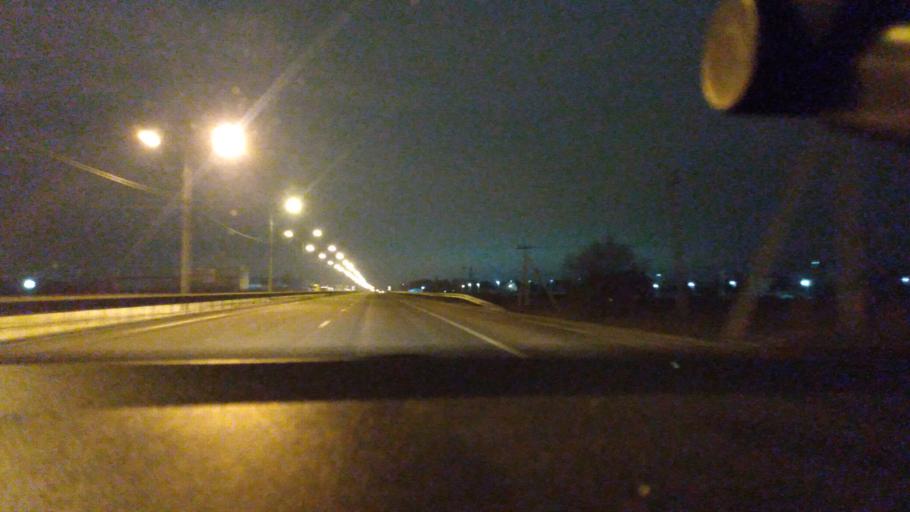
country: RU
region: Moskovskaya
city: Zhukovskiy
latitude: 55.5390
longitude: 38.0914
